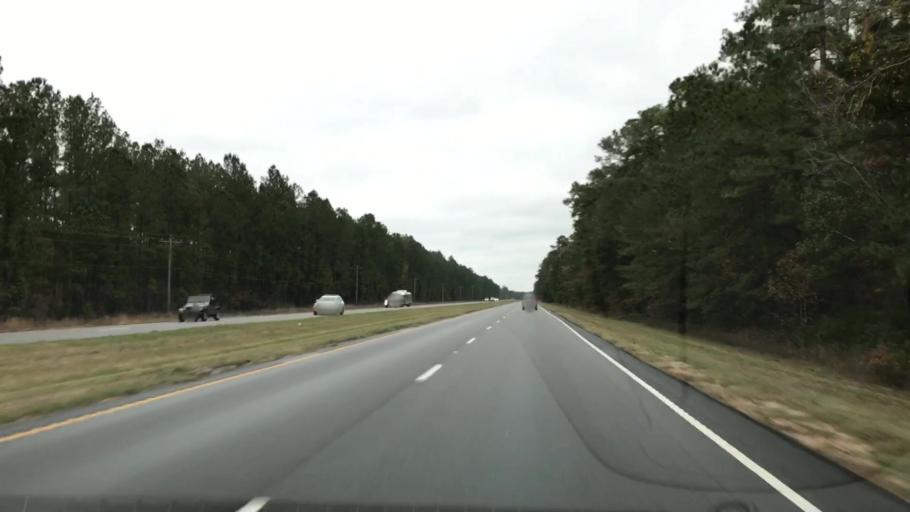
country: US
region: South Carolina
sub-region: Georgetown County
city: Georgetown
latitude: 33.2789
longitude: -79.3510
